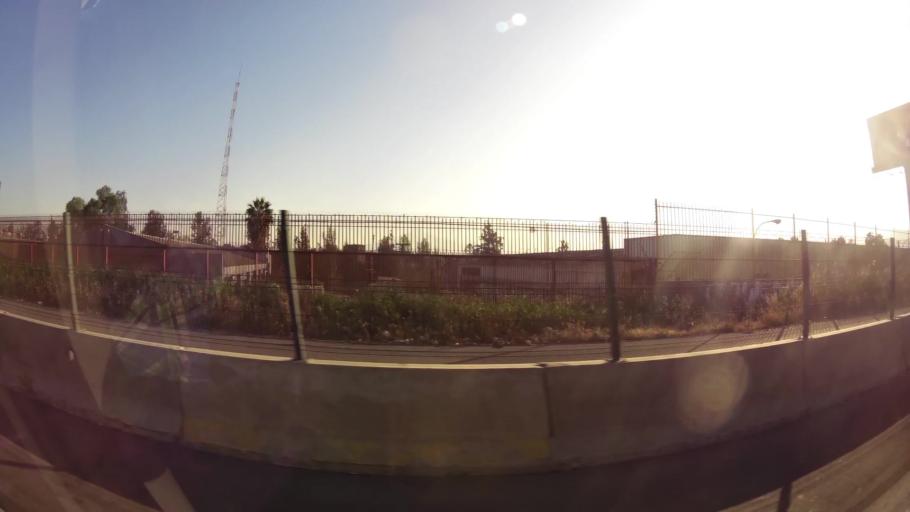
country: CL
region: Santiago Metropolitan
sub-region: Provincia de Santiago
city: Santiago
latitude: -33.4223
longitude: -70.6803
